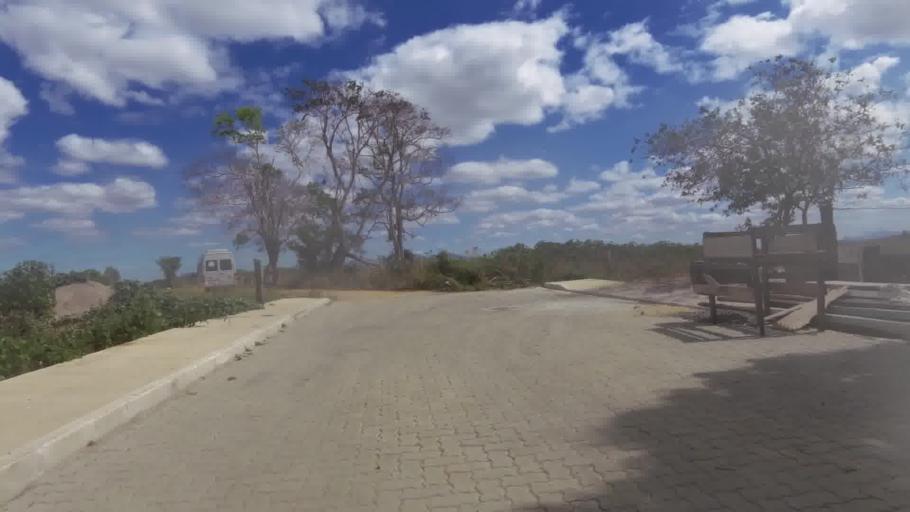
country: BR
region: Espirito Santo
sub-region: Marataizes
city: Marataizes
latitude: -21.1787
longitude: -40.9901
